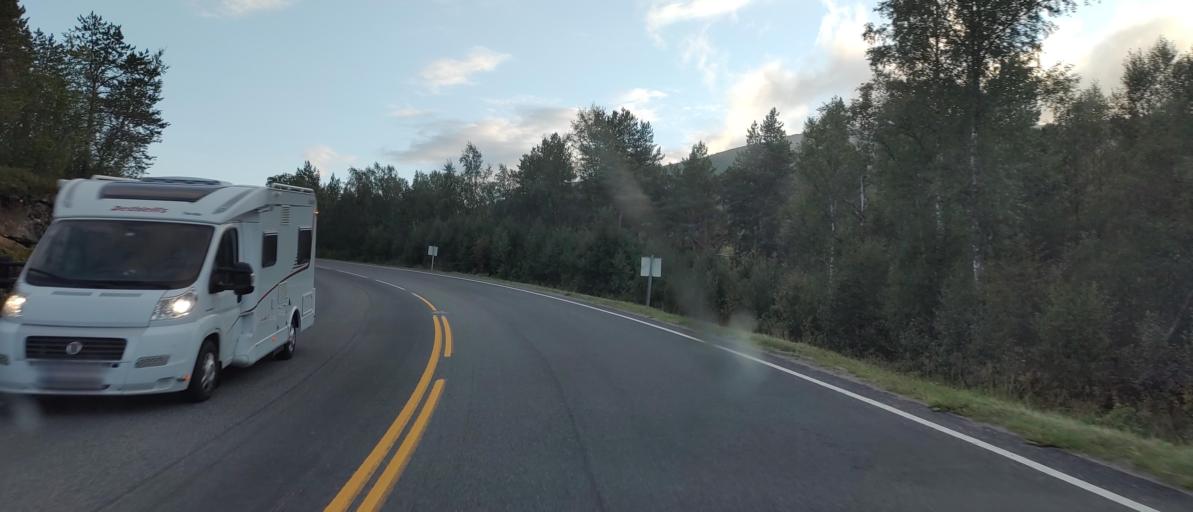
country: NO
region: Nordland
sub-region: Lodingen
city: Lodingen
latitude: 68.2173
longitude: 16.0521
